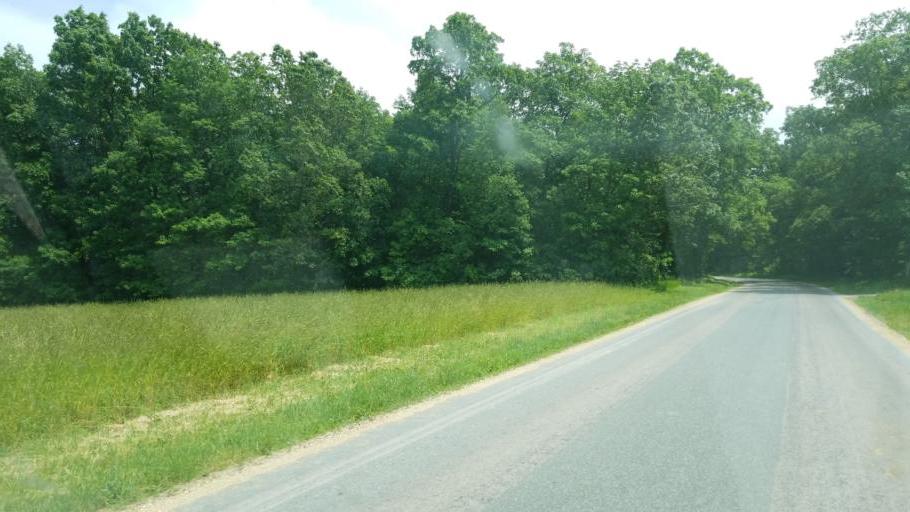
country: US
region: Wisconsin
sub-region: Monroe County
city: Cashton
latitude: 43.6919
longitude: -90.6621
